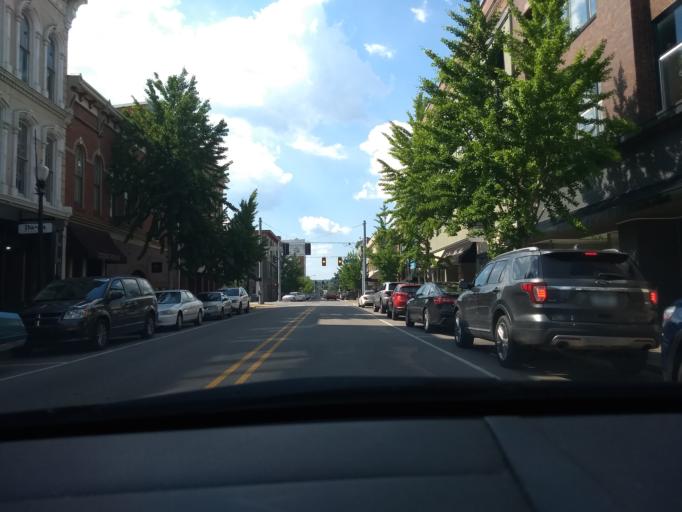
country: US
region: Indiana
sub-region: Floyd County
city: New Albany
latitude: 38.2844
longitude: -85.8222
